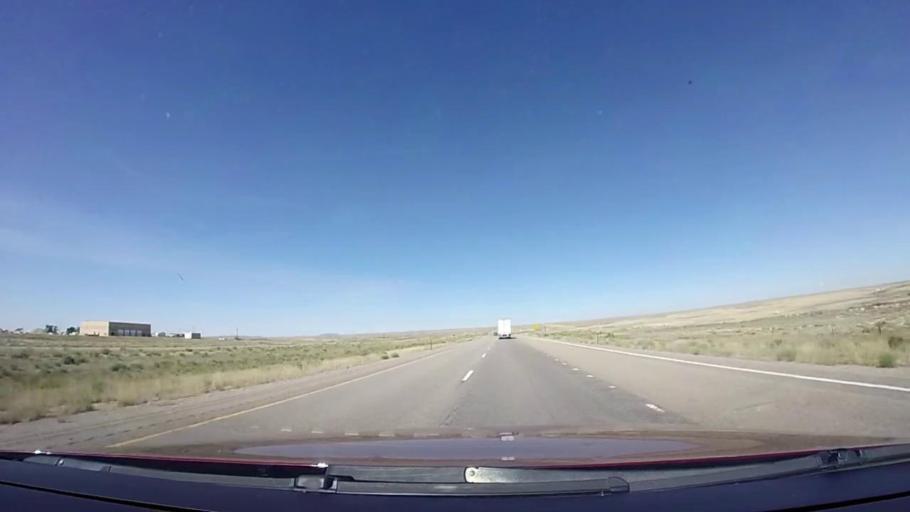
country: US
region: Wyoming
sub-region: Sweetwater County
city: Rock Springs
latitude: 41.6402
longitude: -108.4856
